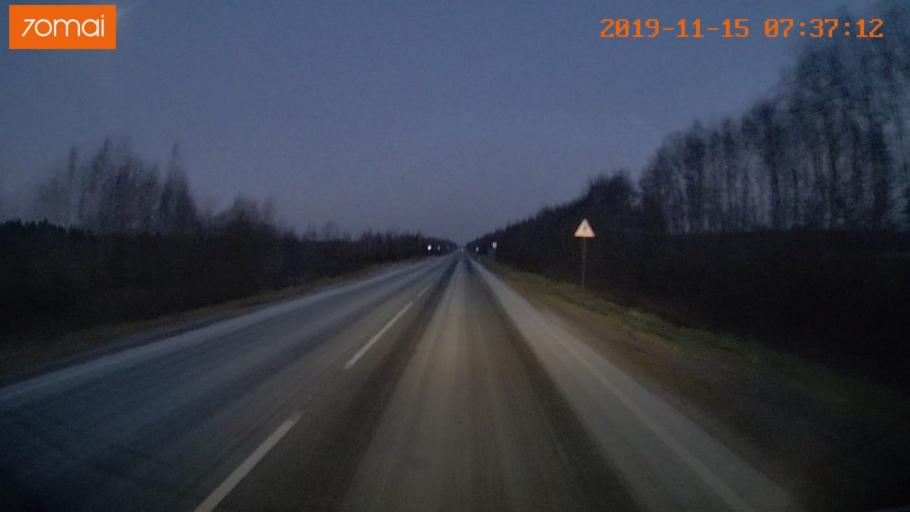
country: RU
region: Vologda
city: Sheksna
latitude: 58.7457
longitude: 38.4245
